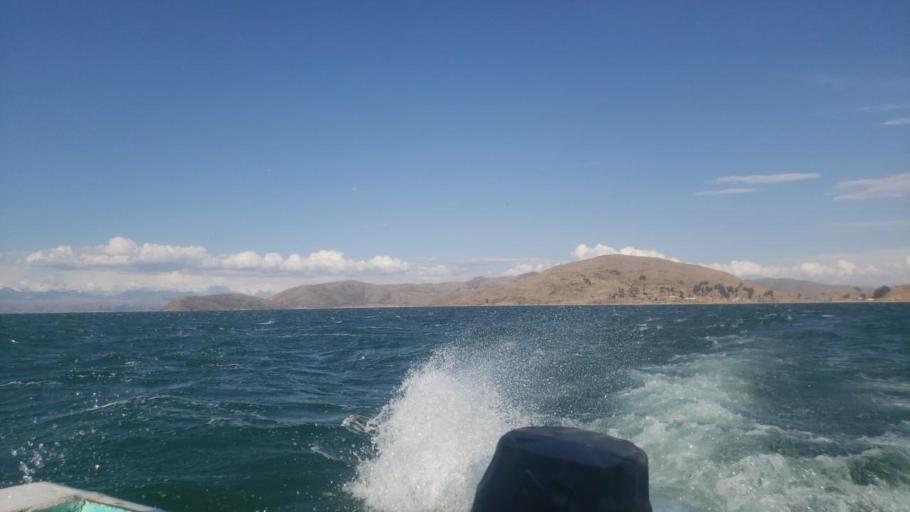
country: BO
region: La Paz
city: Huatajata
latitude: -16.3193
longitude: -68.7373
